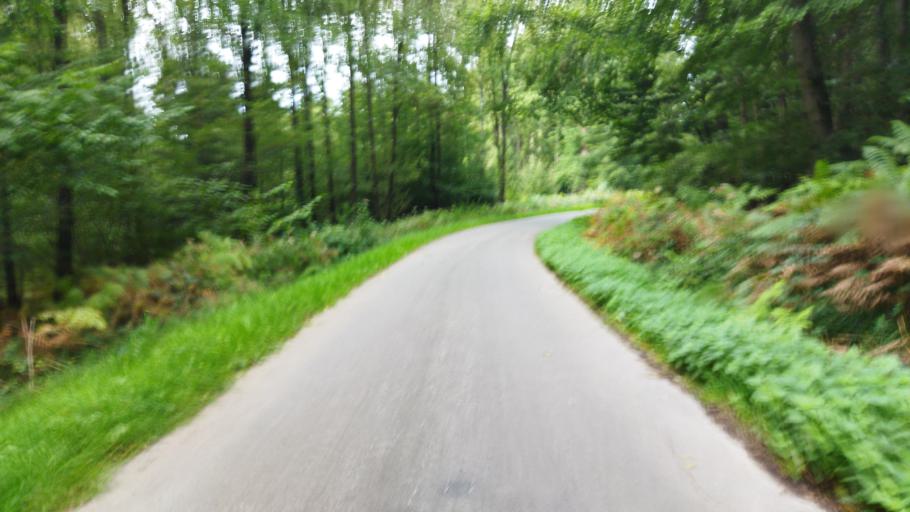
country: DE
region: Lower Saxony
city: Hilter
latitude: 52.1613
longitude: 8.1158
